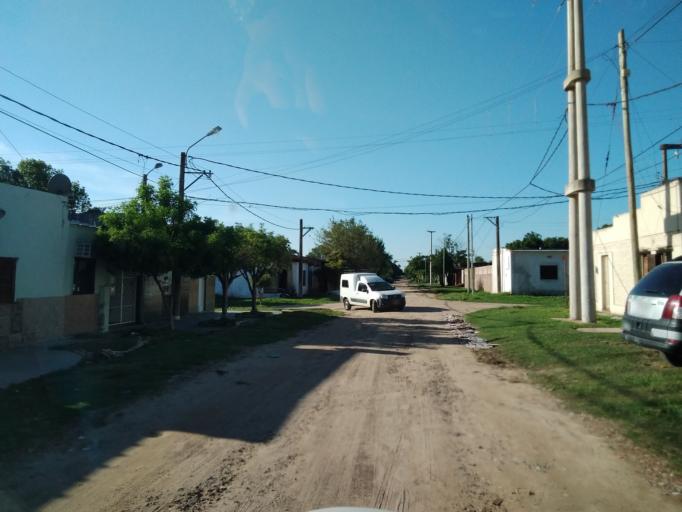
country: AR
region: Corrientes
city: Corrientes
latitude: -27.5034
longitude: -58.7836
